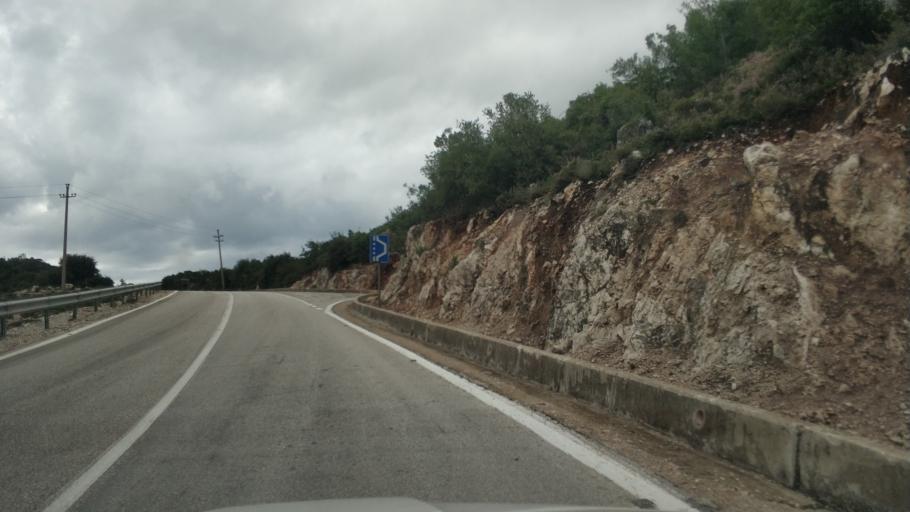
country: AL
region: Vlore
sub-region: Rrethi i Vlores
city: Vranisht
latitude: 40.1427
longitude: 19.6665
